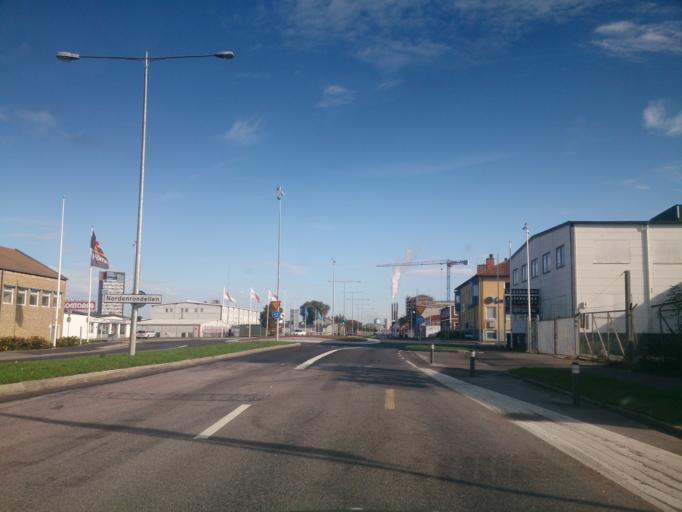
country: SE
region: OEstergoetland
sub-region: Linkopings Kommun
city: Linkoping
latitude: 58.4198
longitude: 15.6056
